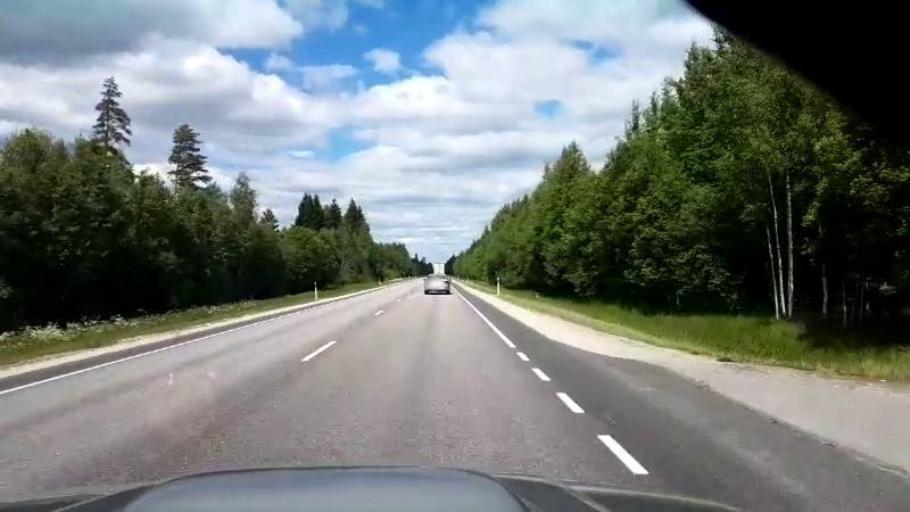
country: EE
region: Paernumaa
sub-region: Halinga vald
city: Parnu-Jaagupi
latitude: 58.7151
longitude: 24.4238
